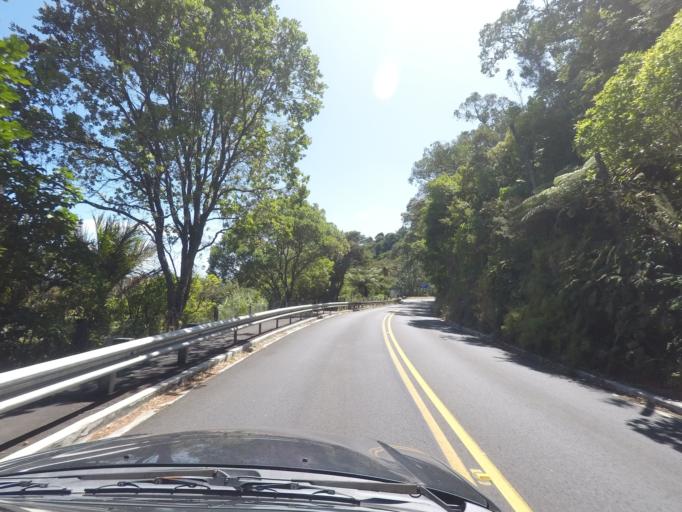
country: NZ
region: Auckland
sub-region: Auckland
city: Titirangi
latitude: -36.9378
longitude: 174.6458
